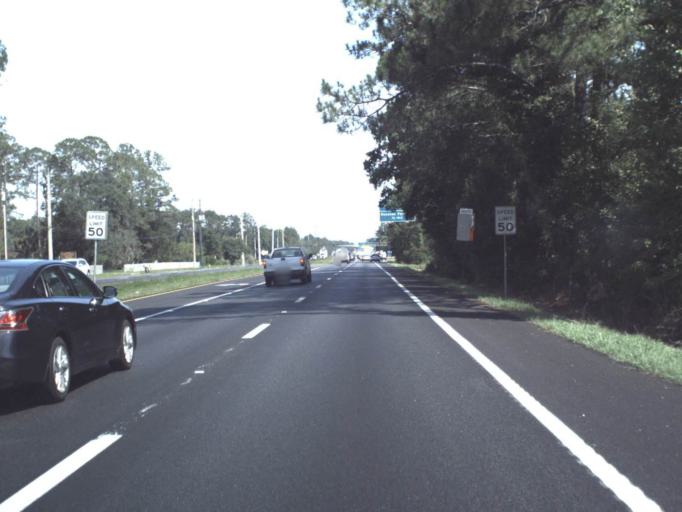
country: US
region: Florida
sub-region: Saint Johns County
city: Palm Valley
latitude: 30.1076
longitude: -81.4821
